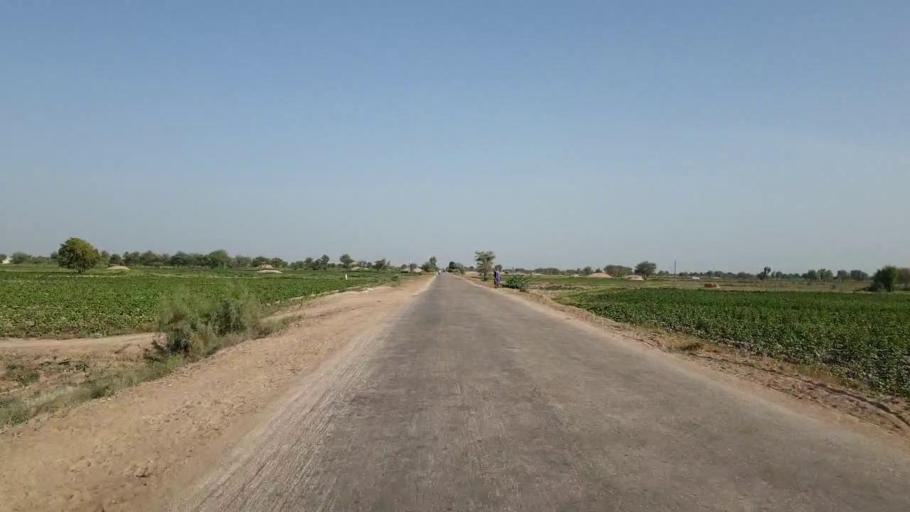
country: PK
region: Sindh
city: Nawabshah
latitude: 26.1379
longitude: 68.4531
